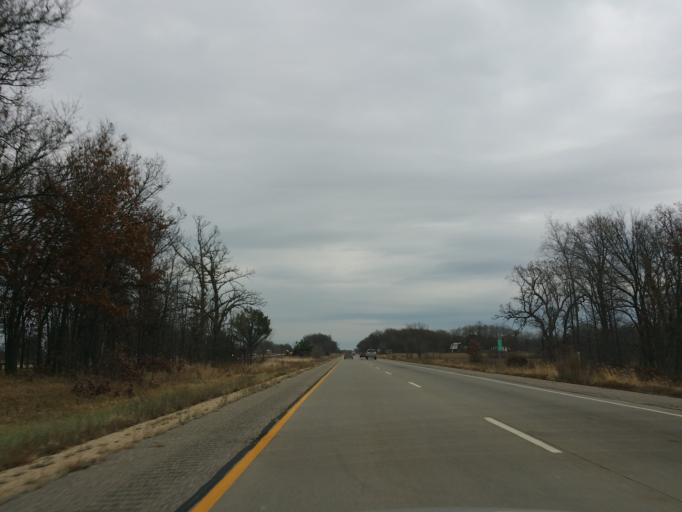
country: US
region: Wisconsin
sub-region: Juneau County
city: New Lisbon
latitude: 43.9017
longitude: -90.1977
